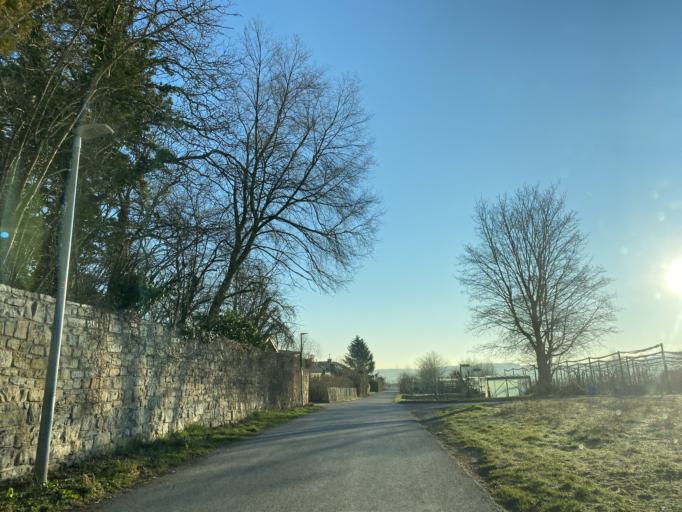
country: DE
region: Baden-Wuerttemberg
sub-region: Regierungsbezirk Stuttgart
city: Eberdingen
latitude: 48.8925
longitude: 8.9412
